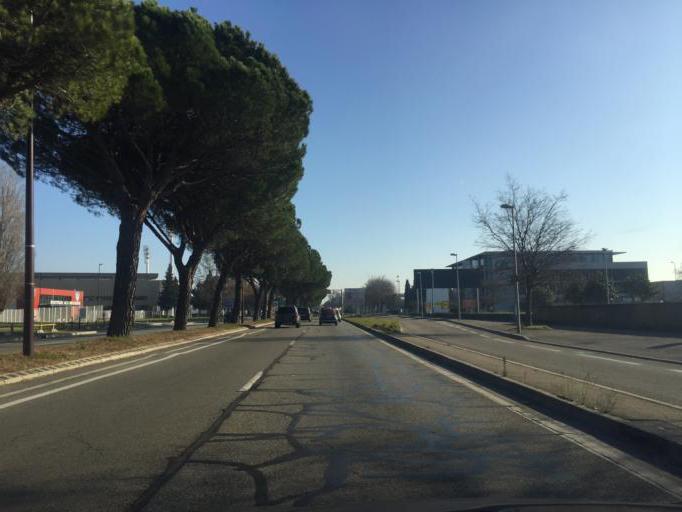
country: FR
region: Provence-Alpes-Cote d'Azur
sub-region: Departement du Vaucluse
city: Montfavet
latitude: 43.9285
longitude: 4.8411
